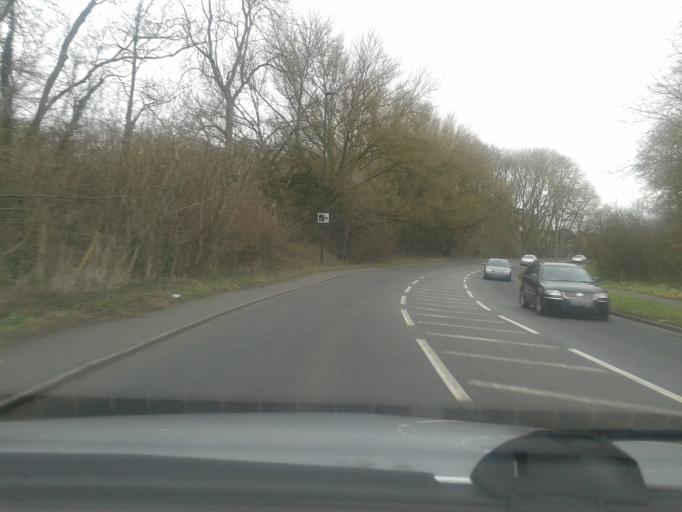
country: GB
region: England
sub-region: South Gloucestershire
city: Winterbourne
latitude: 51.5196
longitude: -2.4787
